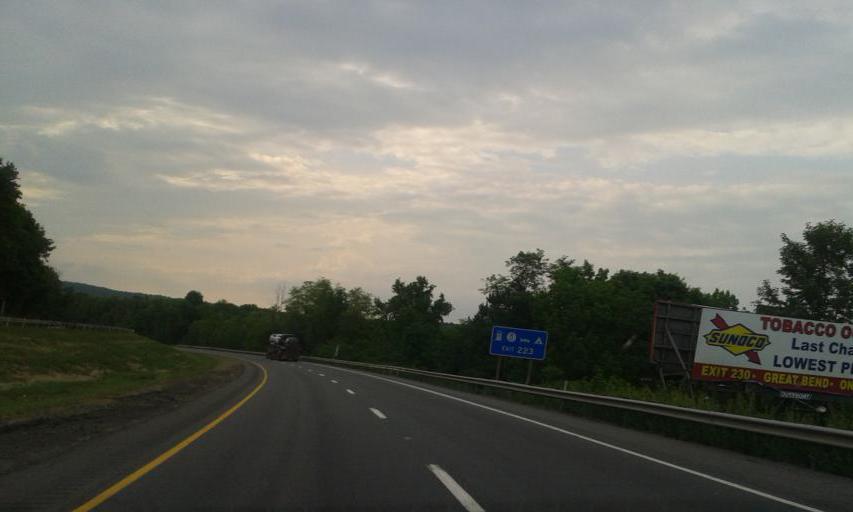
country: US
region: Pennsylvania
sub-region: Susquehanna County
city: Hallstead
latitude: 41.8562
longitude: -75.6845
